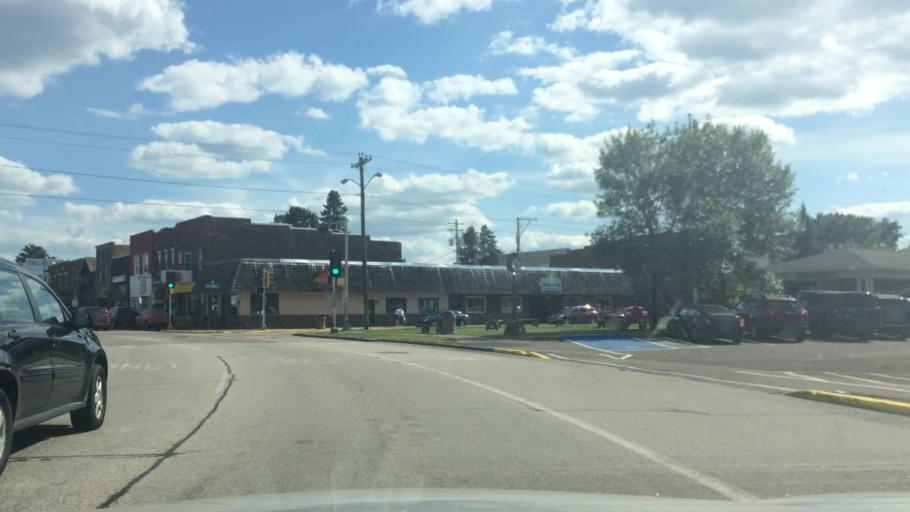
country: US
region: Wisconsin
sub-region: Vilas County
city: Lac du Flambeau
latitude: 45.8719
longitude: -89.7100
